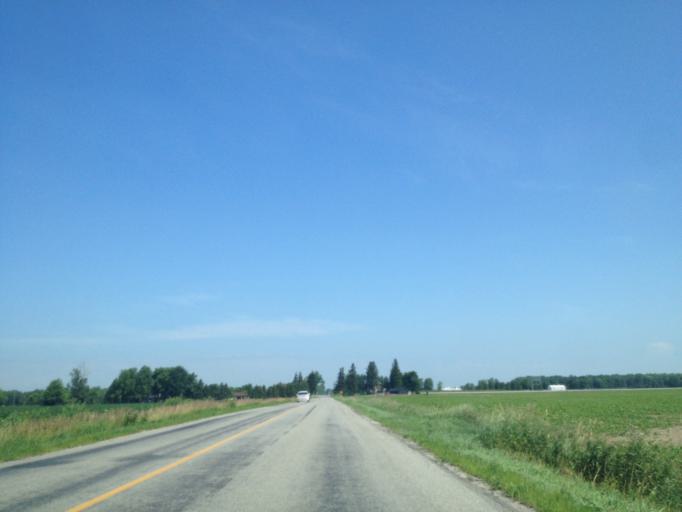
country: CA
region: Ontario
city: London
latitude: 43.1375
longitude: -81.2111
